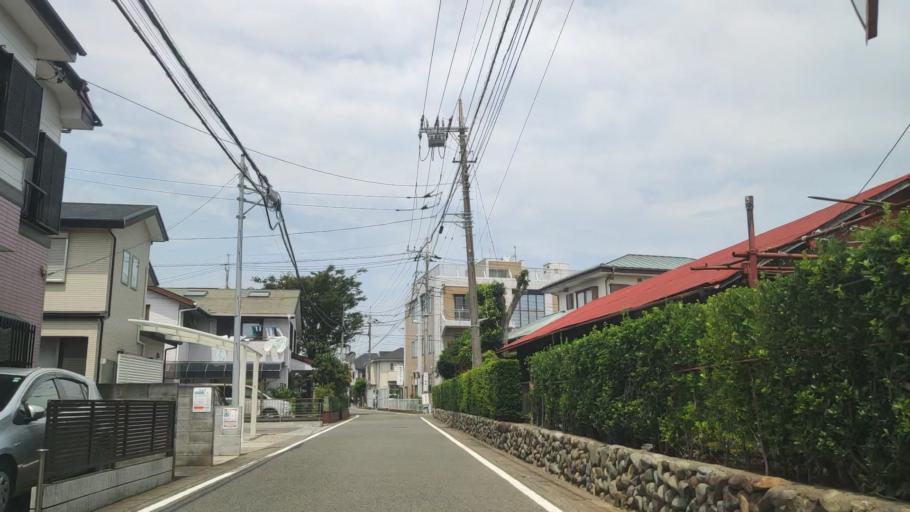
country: JP
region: Kanagawa
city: Atsugi
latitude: 35.4458
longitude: 139.3972
